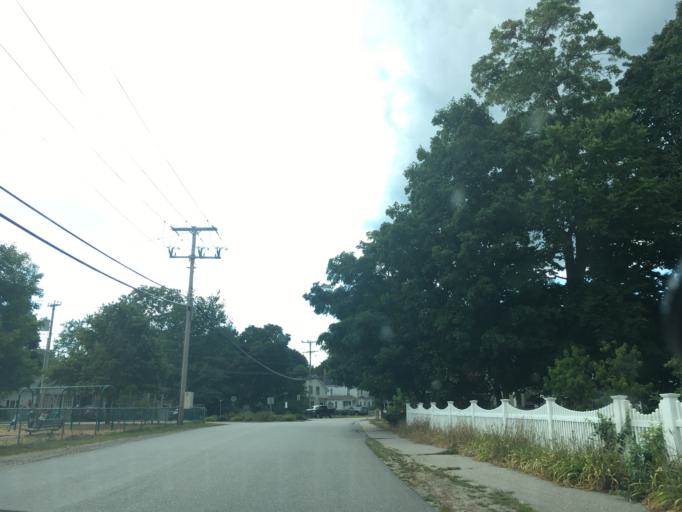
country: US
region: New Hampshire
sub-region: Rockingham County
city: Exeter
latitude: 42.9801
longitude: -70.9626
